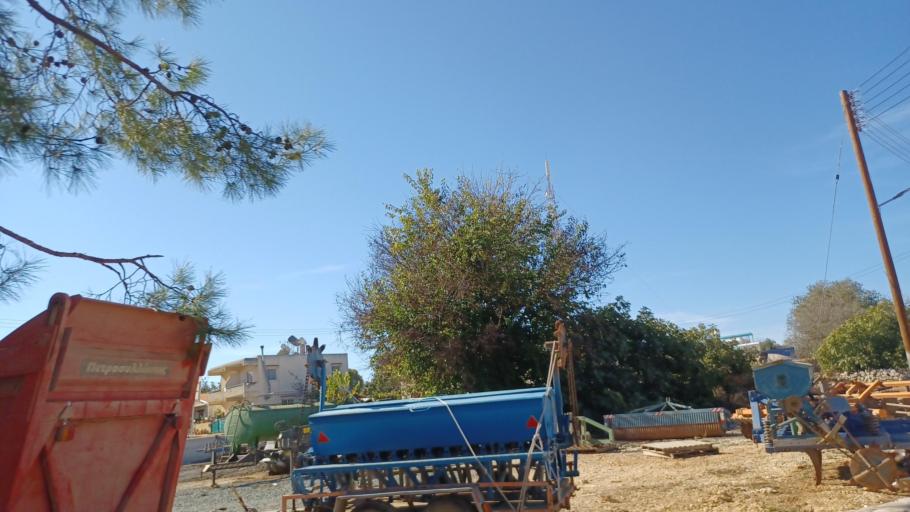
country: CY
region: Pafos
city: Pegeia
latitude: 34.9593
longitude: 32.3981
